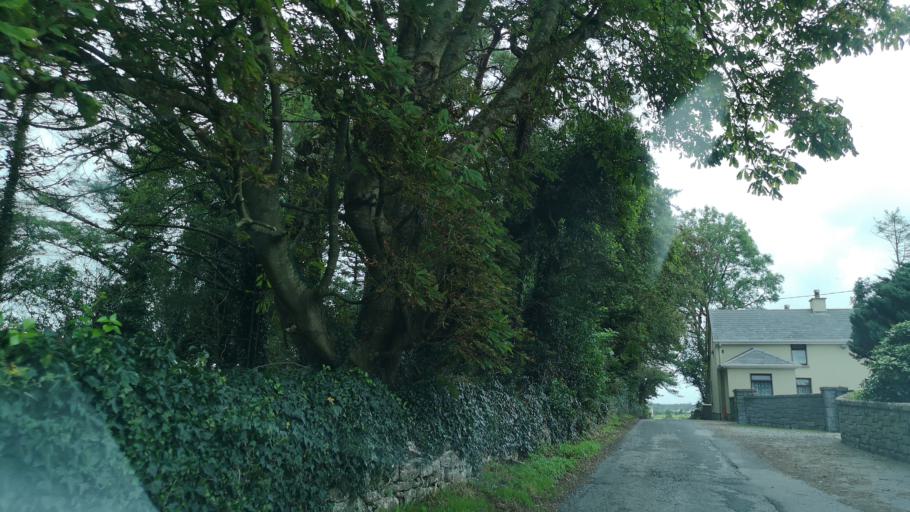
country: IE
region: Connaught
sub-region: County Galway
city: Athenry
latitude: 53.3120
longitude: -8.7451
